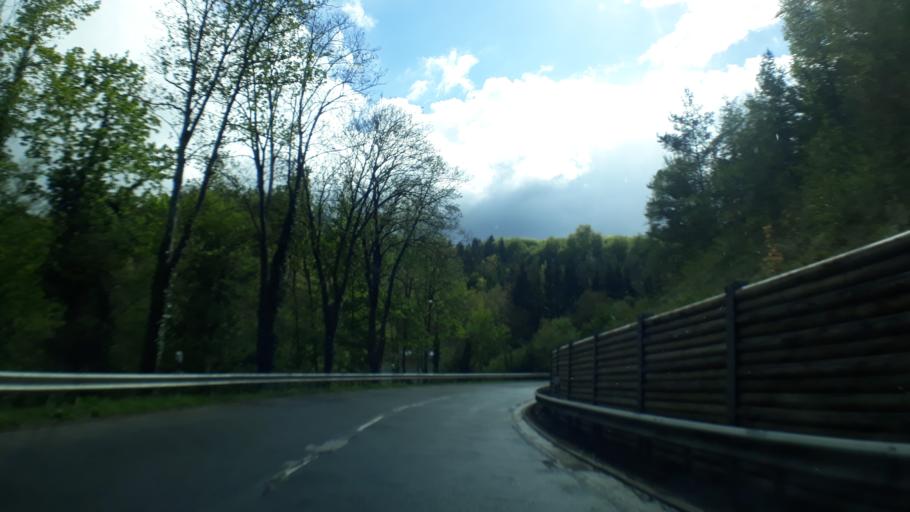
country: DE
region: North Rhine-Westphalia
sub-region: Regierungsbezirk Koln
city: Kall
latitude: 50.5191
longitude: 6.5624
